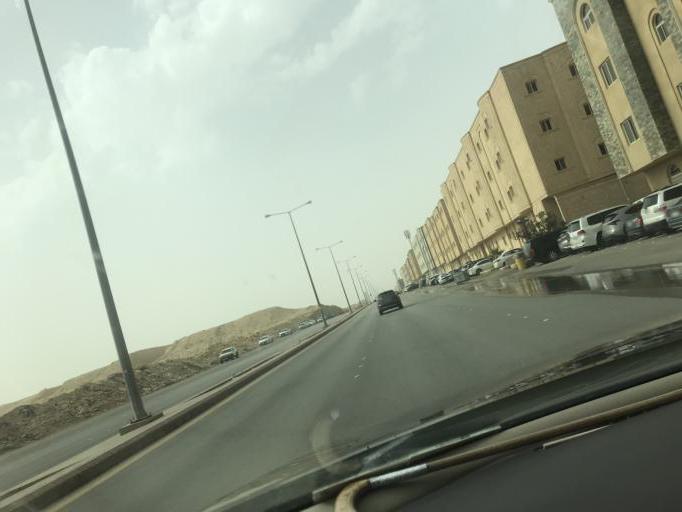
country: SA
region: Ar Riyad
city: Riyadh
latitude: 24.7920
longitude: 46.6695
